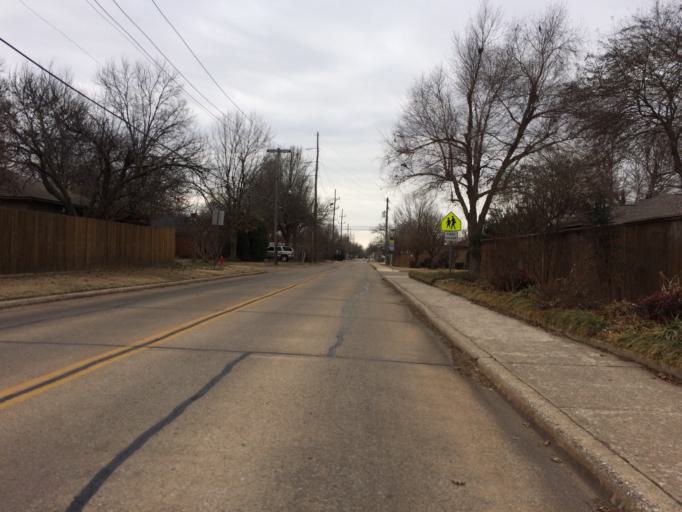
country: US
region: Oklahoma
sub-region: Cleveland County
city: Norman
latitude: 35.2158
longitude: -97.4634
